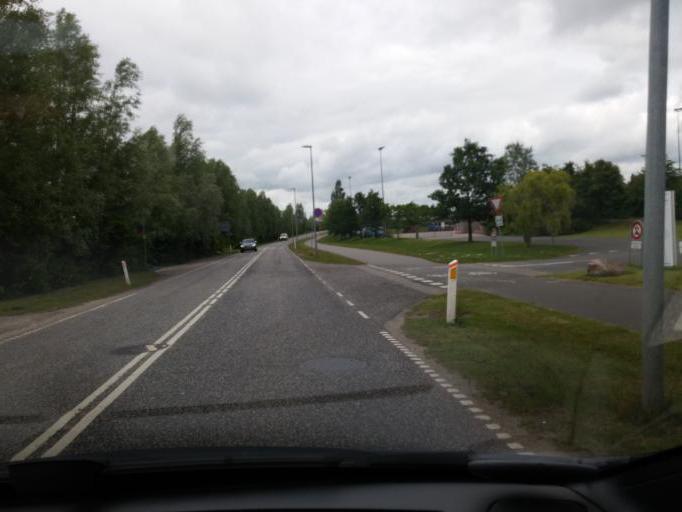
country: DK
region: Capital Region
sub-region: Hillerod Kommune
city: Hillerod
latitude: 55.9193
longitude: 12.2816
